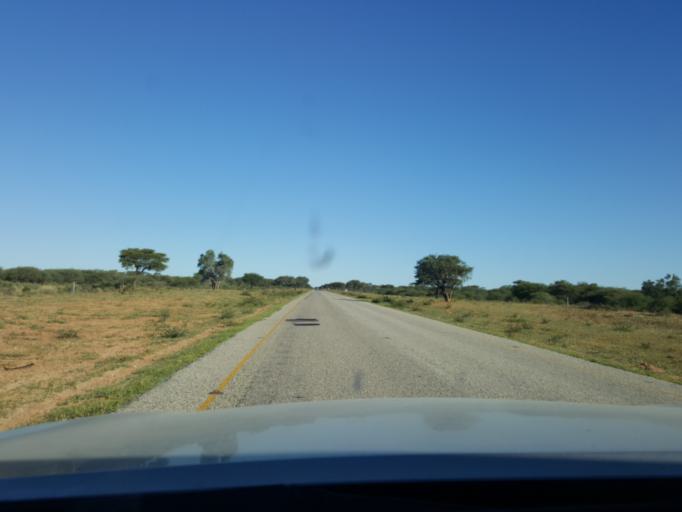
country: BW
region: Kgalagadi
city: Kang
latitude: -24.0307
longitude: 23.0424
